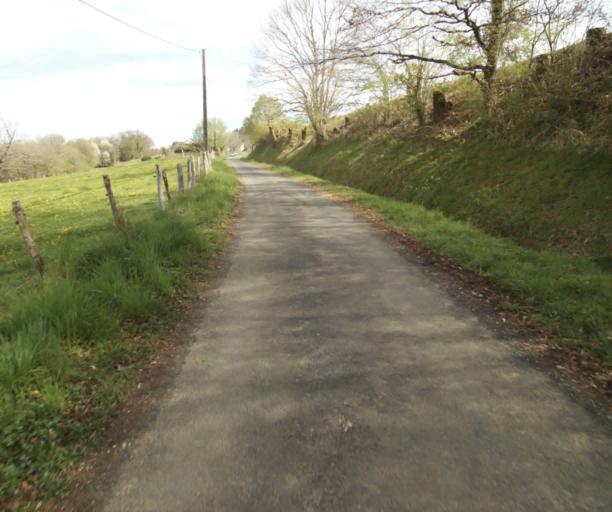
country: FR
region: Limousin
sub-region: Departement de la Correze
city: Laguenne
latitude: 45.2510
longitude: 1.8059
